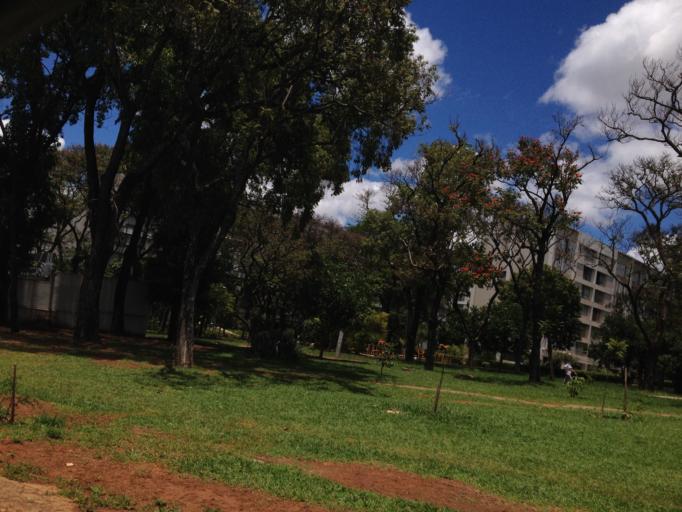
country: BR
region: Federal District
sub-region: Brasilia
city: Brasilia
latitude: -15.8165
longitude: -47.9061
